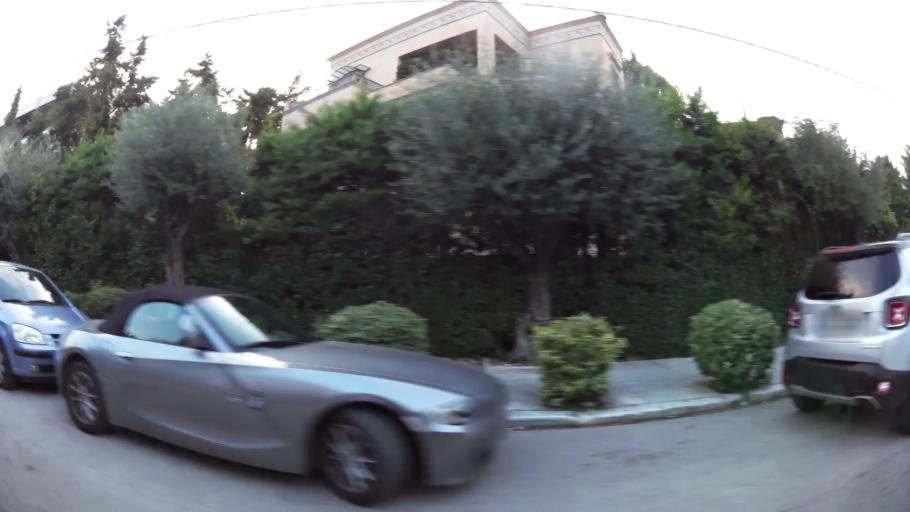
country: GR
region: Attica
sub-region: Nomarchia Athinas
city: Filothei
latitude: 38.0248
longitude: 23.7851
